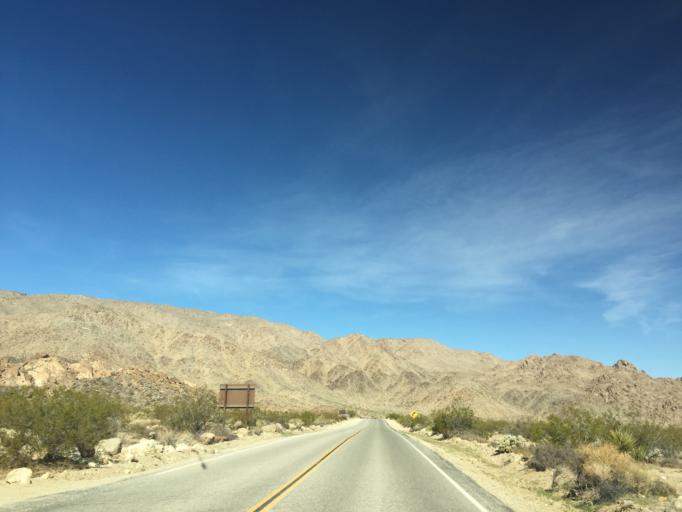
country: US
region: California
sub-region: San Bernardino County
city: Twentynine Palms
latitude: 34.0724
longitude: -116.0325
